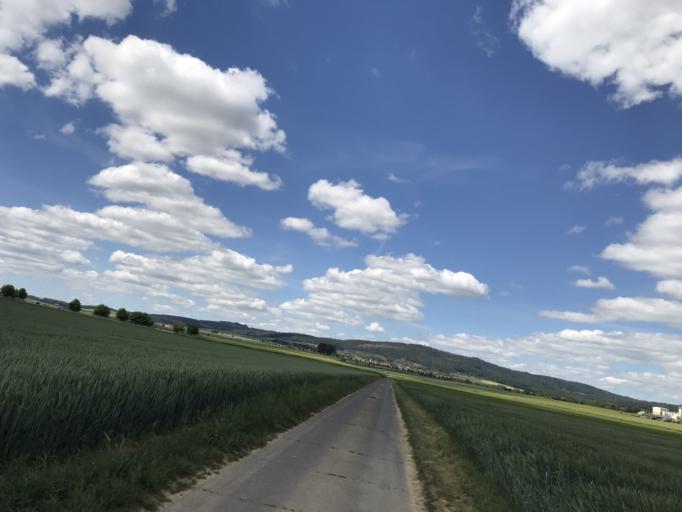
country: DE
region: Hesse
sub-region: Regierungsbezirk Darmstadt
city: Ober-Morlen
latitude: 50.3934
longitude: 8.6792
